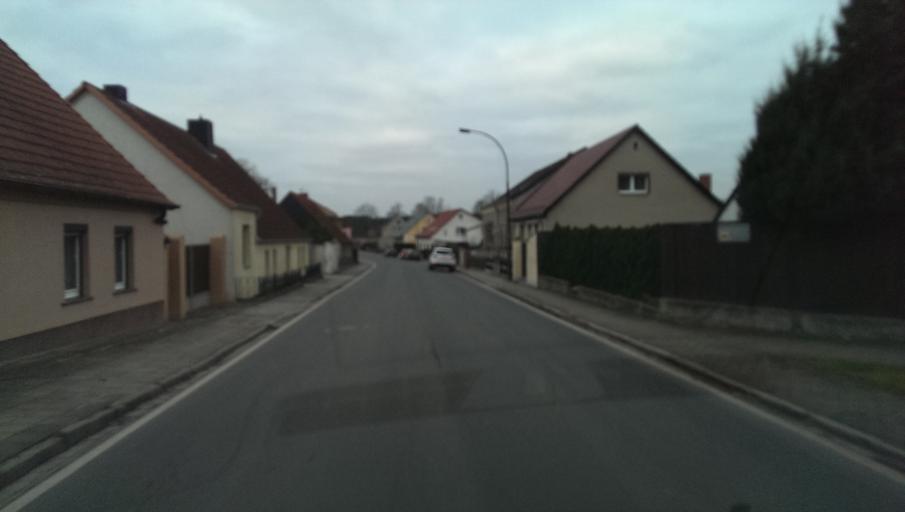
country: DE
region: Brandenburg
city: Sperenberg
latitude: 52.1424
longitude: 13.3642
